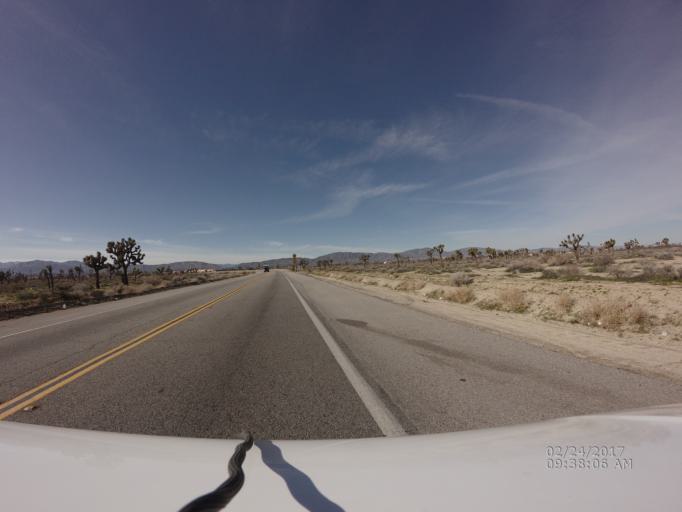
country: US
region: California
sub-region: Los Angeles County
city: Palmdale
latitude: 34.5838
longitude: -118.0430
